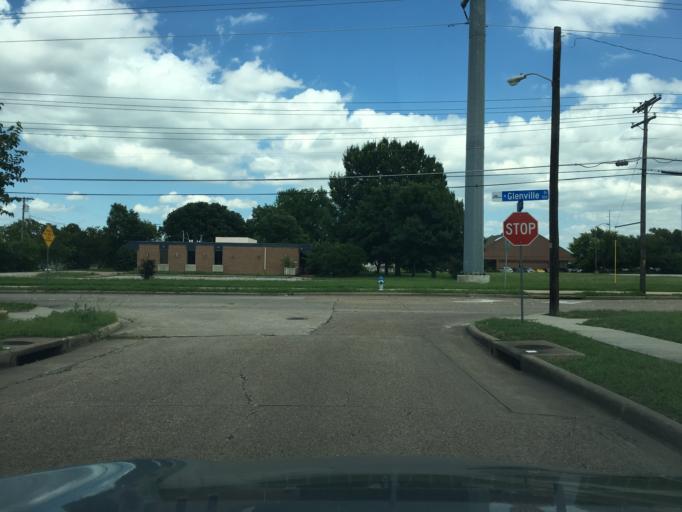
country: US
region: Texas
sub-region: Dallas County
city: Richardson
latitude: 32.9466
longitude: -96.7053
